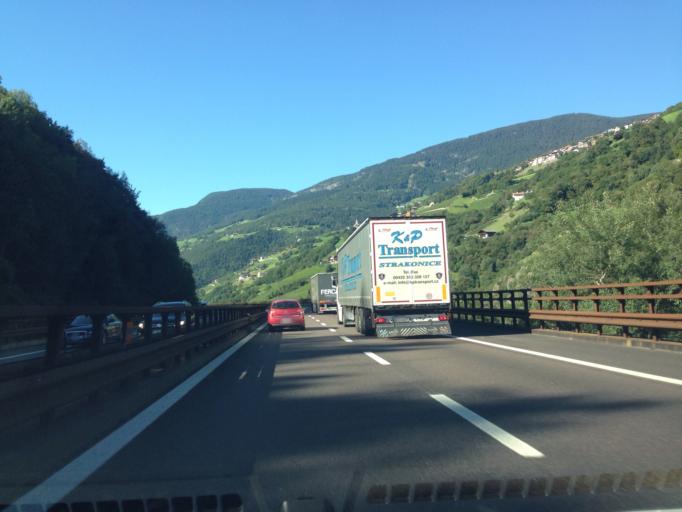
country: IT
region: Trentino-Alto Adige
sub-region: Bolzano
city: Chiusa
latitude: 46.6304
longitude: 11.5538
